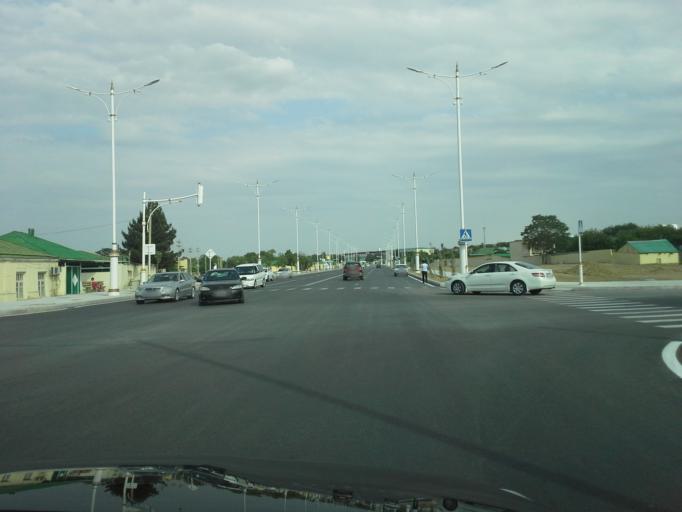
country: TM
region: Ahal
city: Ashgabat
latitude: 37.9612
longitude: 58.3349
